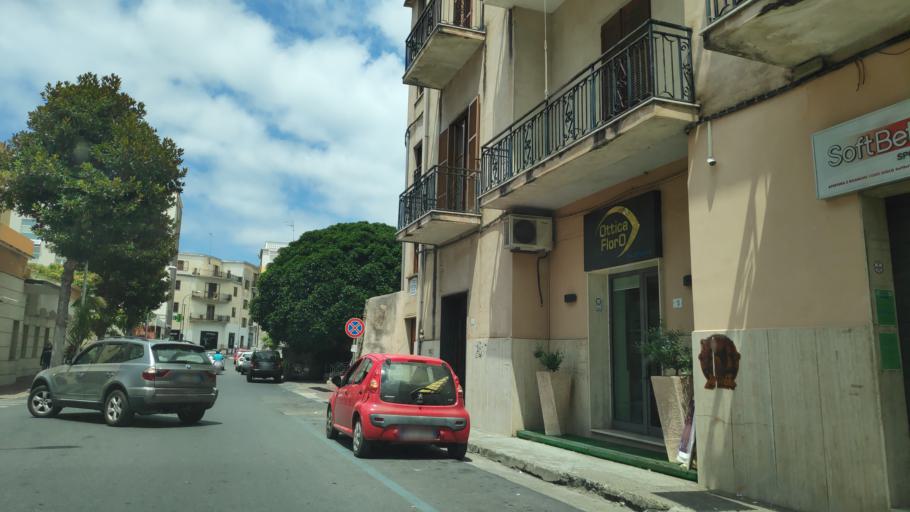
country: IT
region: Calabria
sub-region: Provincia di Cosenza
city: Paola
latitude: 39.3582
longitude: 16.0415
